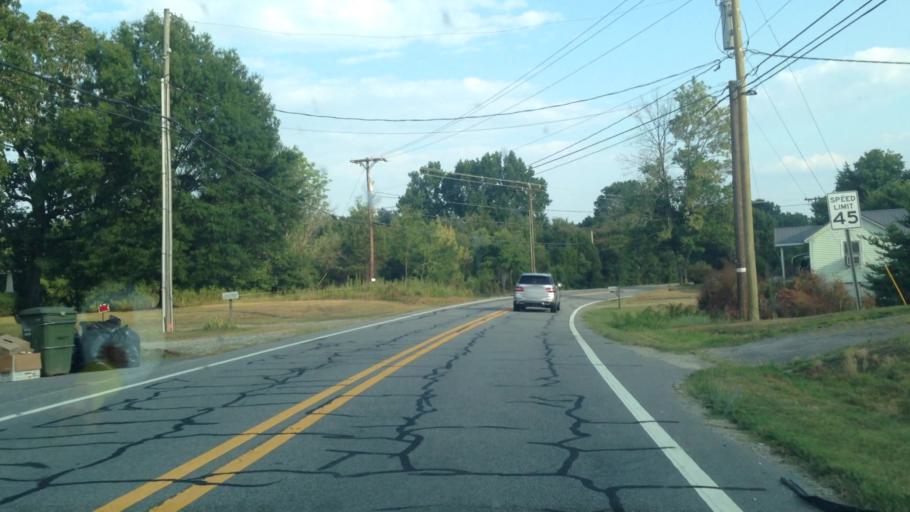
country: US
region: North Carolina
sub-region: Guilford County
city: High Point
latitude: 35.9872
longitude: -80.0661
